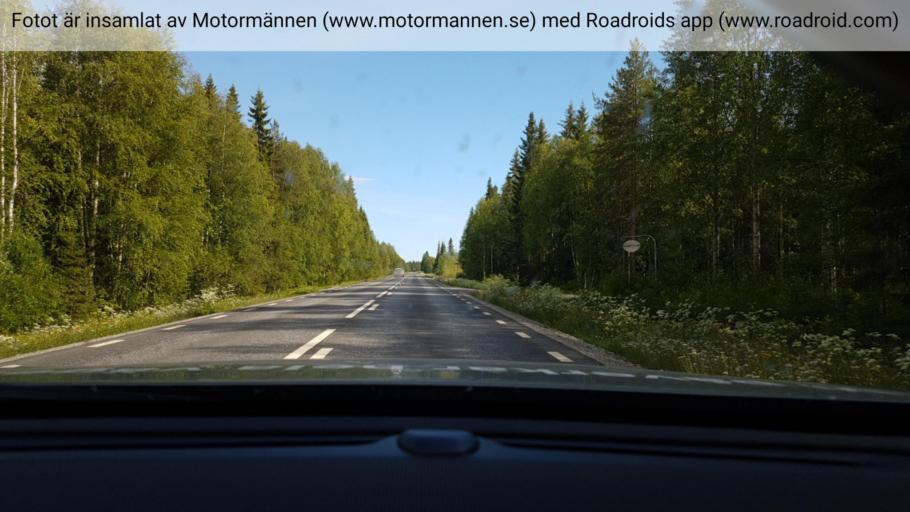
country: SE
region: Vaesterbotten
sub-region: Lycksele Kommun
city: Soderfors
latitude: 64.8237
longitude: 18.0581
